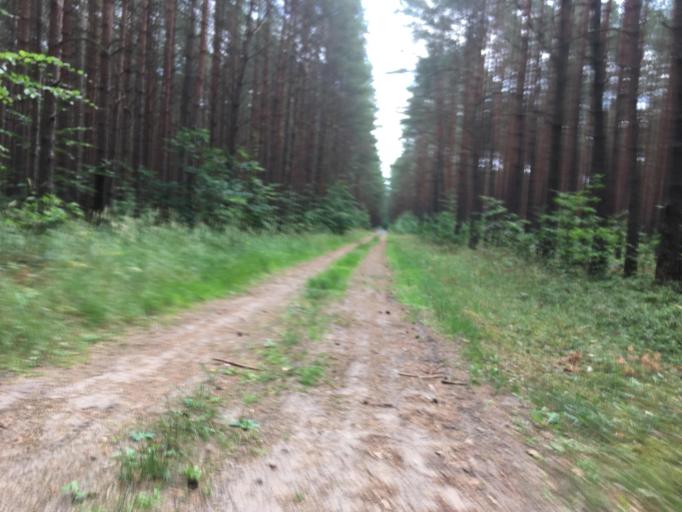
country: DE
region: Brandenburg
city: Friedrichswalde
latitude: 53.0145
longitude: 13.7300
